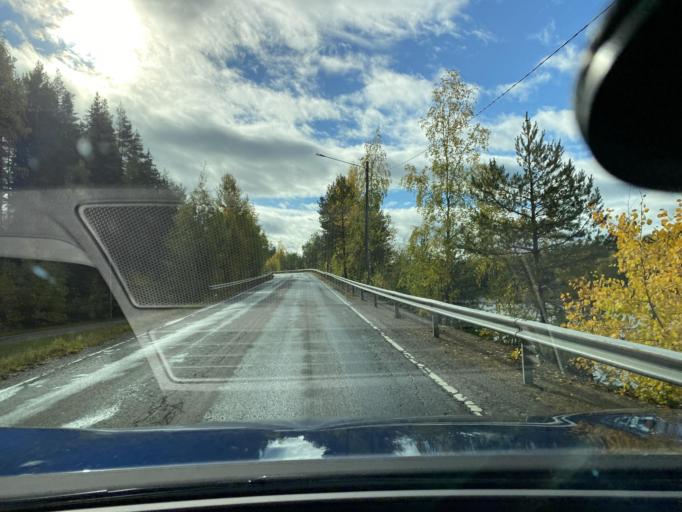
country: FI
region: Pirkanmaa
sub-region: Tampere
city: Nokia
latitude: 61.4793
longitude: 23.3410
